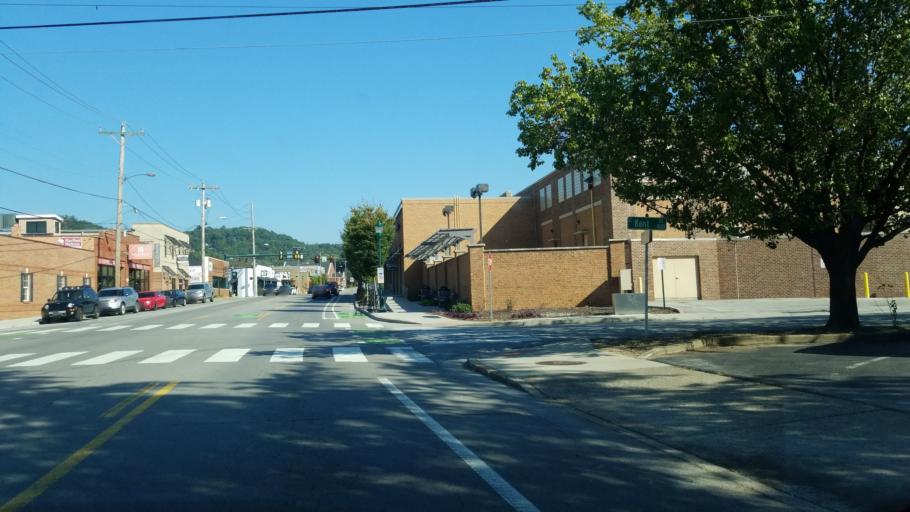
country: US
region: Tennessee
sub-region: Hamilton County
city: Chattanooga
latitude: 35.0643
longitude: -85.3088
